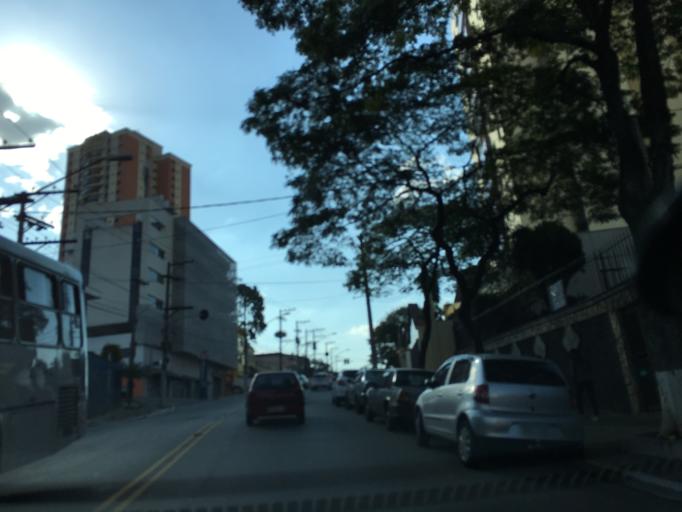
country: BR
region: Sao Paulo
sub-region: Sao Paulo
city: Sao Paulo
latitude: -23.4802
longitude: -46.6323
